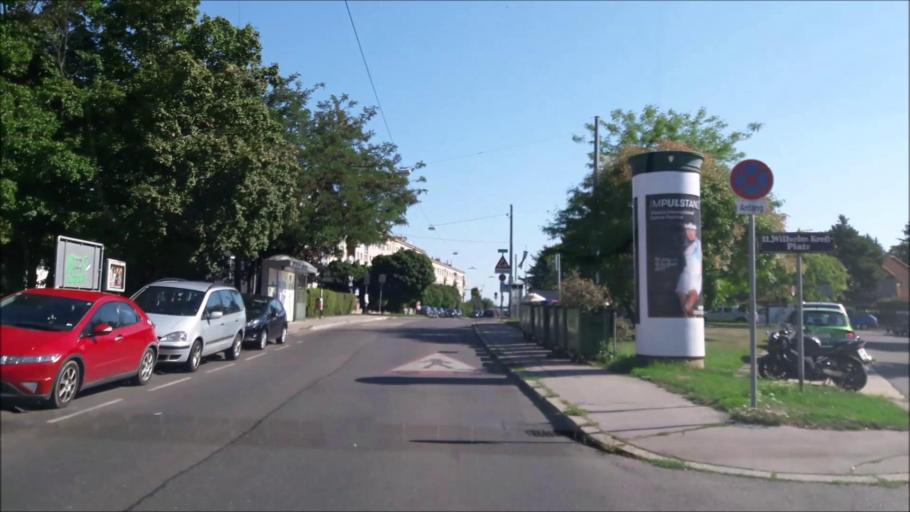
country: AT
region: Lower Austria
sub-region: Politischer Bezirk Wien-Umgebung
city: Schwechat
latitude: 48.1600
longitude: 16.4266
